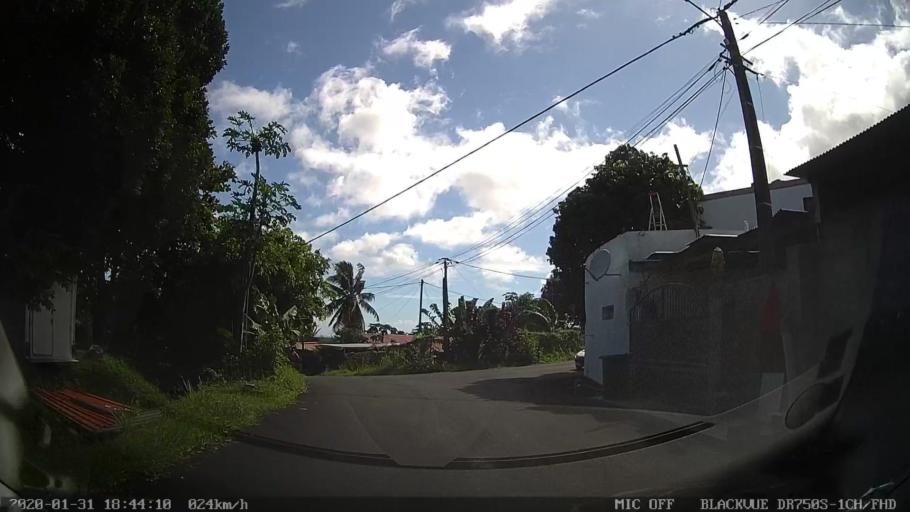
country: RE
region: Reunion
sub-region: Reunion
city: Sainte-Marie
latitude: -20.9155
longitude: 55.5318
